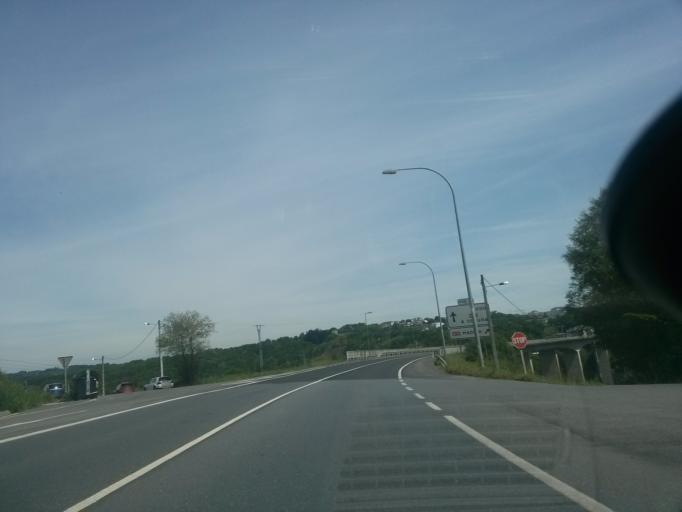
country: ES
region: Galicia
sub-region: Provincia de Lugo
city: Lugo
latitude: 43.0038
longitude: -7.5831
